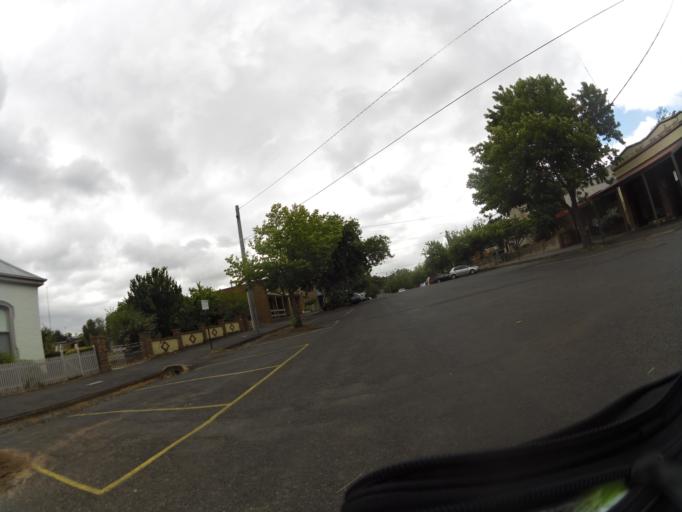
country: AU
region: Victoria
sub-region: Mount Alexander
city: Castlemaine
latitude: -37.0631
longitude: 144.2158
